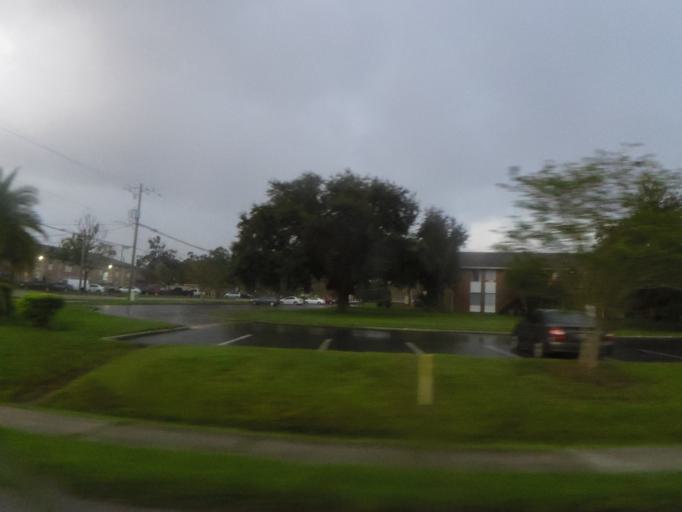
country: US
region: Florida
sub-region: Duval County
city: Jacksonville
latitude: 30.2488
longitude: -81.6219
